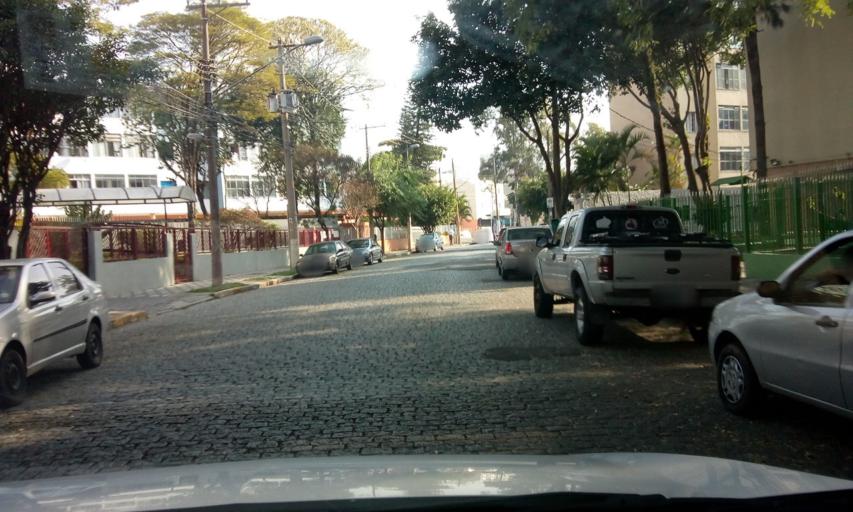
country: BR
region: Sao Paulo
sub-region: Sao Paulo
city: Sao Paulo
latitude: -23.5540
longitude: -46.5925
